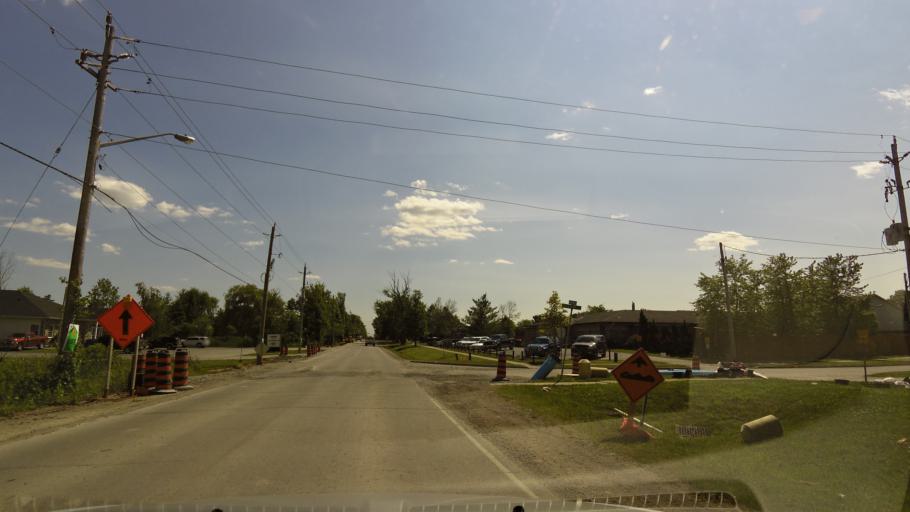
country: CA
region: Ontario
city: Brantford
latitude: 43.0745
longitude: -80.1143
